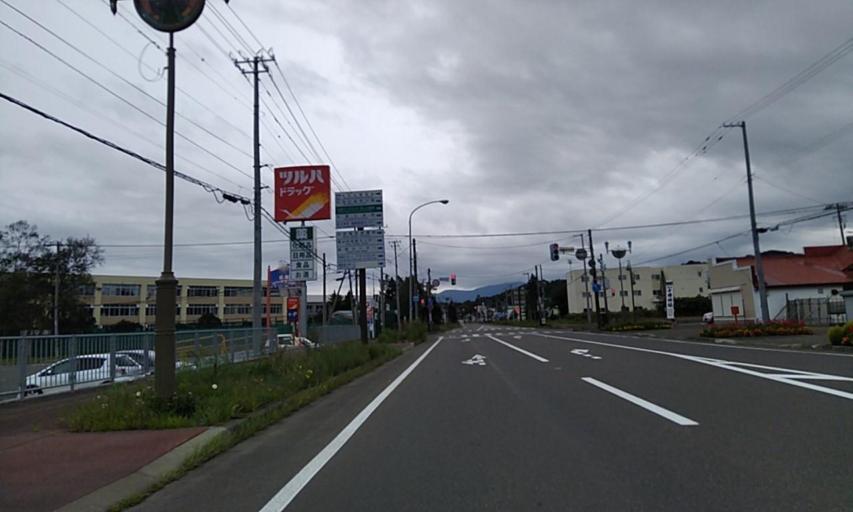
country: JP
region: Hokkaido
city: Obihiro
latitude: 42.2984
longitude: 143.3146
